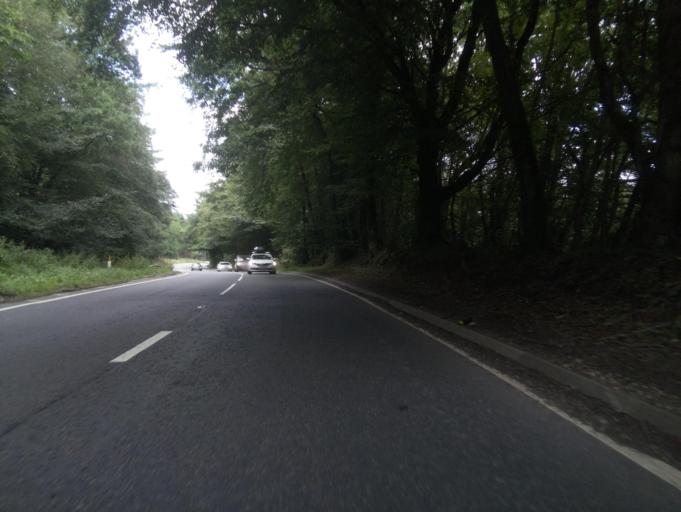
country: GB
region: England
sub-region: Devon
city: Exminster
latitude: 50.6421
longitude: -3.5397
